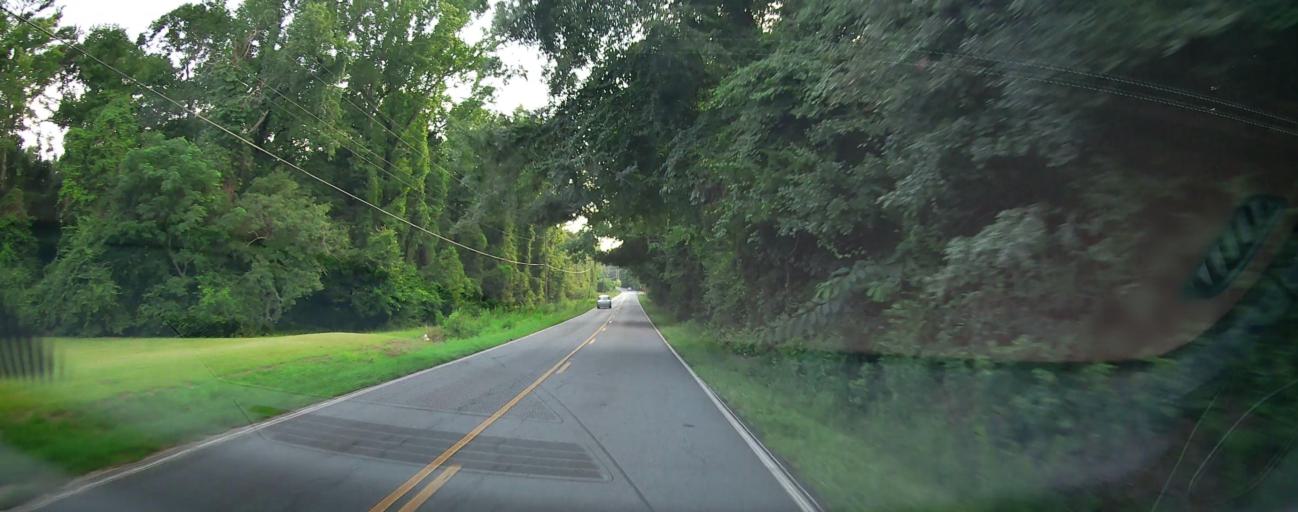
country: US
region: Georgia
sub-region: Peach County
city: Byron
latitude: 32.7237
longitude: -83.7629
